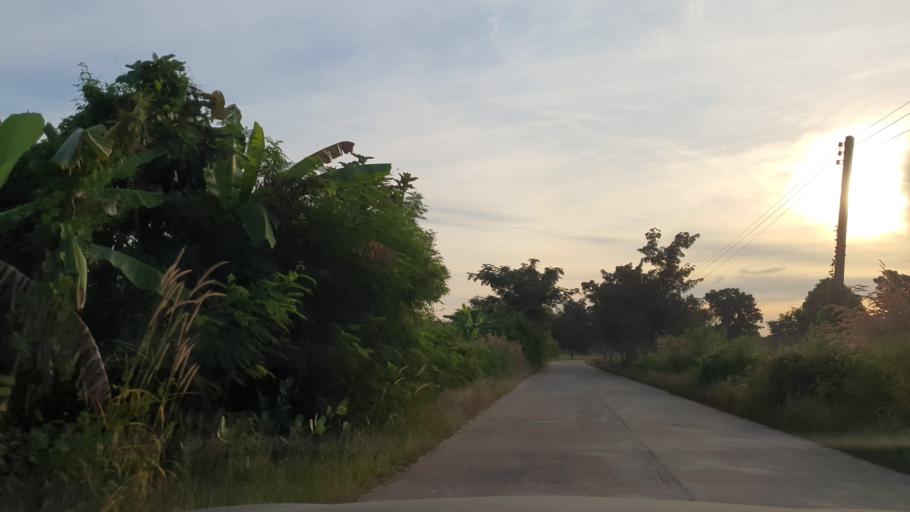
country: TH
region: Nakhon Sawan
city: Krok Phra
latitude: 15.6629
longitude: 100.0136
